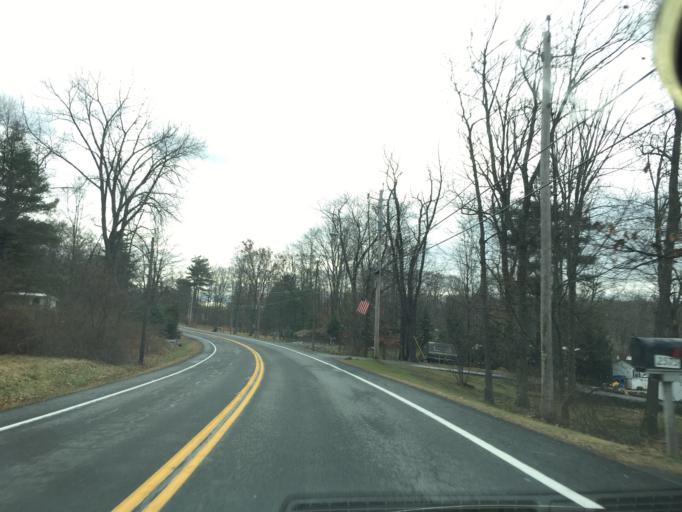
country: US
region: New York
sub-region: Rensselaer County
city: Averill Park
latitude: 42.6230
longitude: -73.5278
